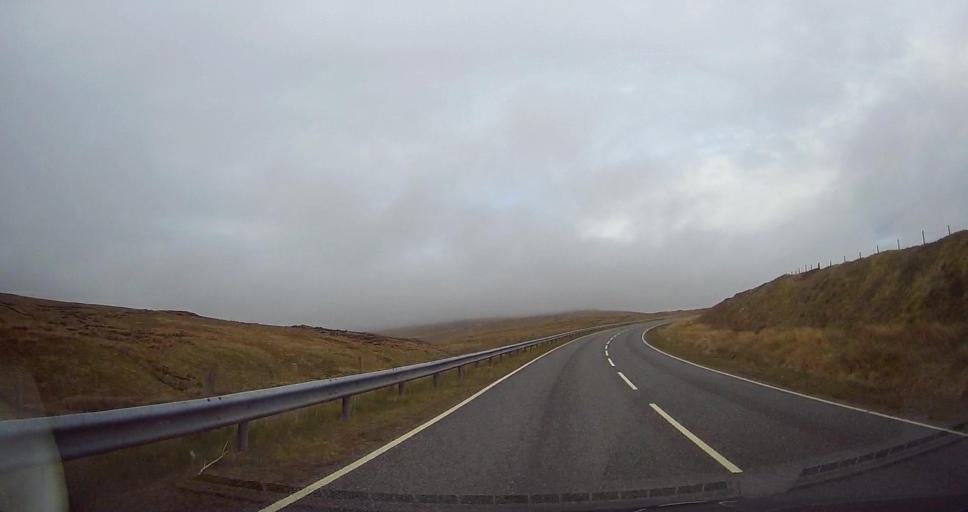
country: GB
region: Scotland
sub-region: Shetland Islands
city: Sandwick
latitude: 60.0050
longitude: -1.2784
